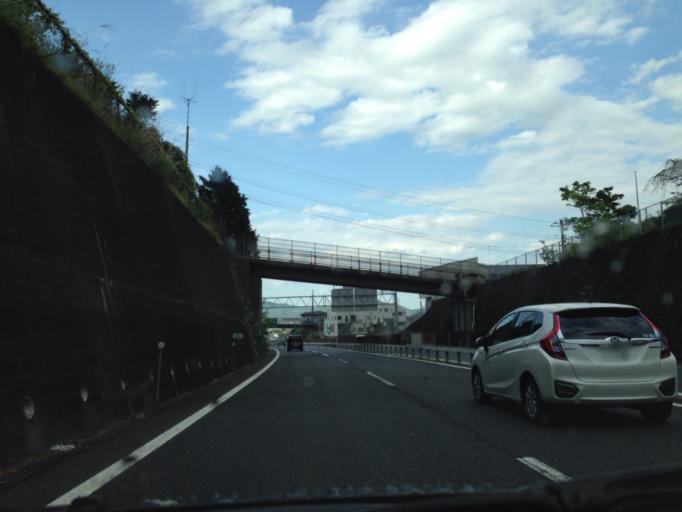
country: JP
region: Kanagawa
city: Odawara
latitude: 35.2634
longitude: 139.1453
